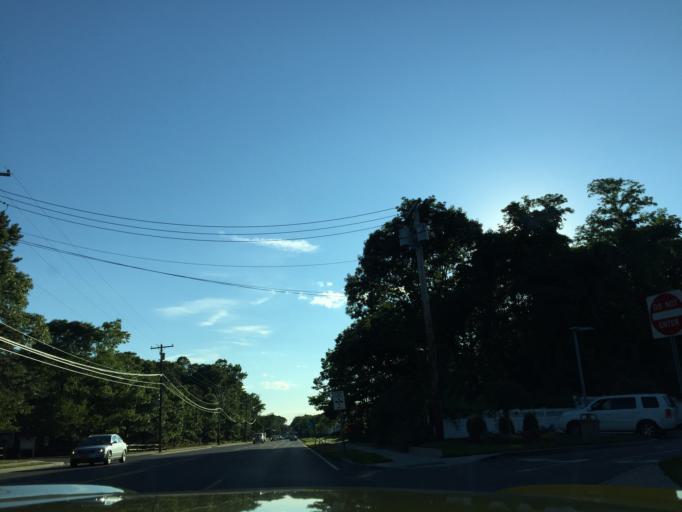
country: US
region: New York
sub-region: Suffolk County
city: Riverhead
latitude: 40.9363
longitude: -72.6543
